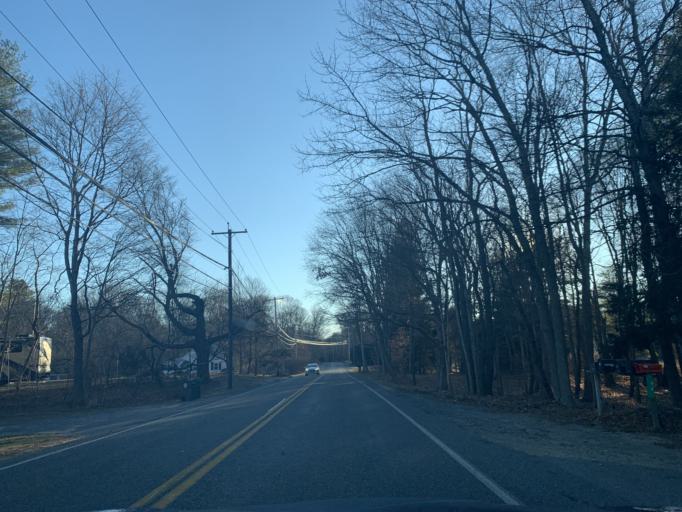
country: US
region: Massachusetts
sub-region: Bristol County
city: Rehoboth
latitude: 41.8928
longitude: -71.2249
